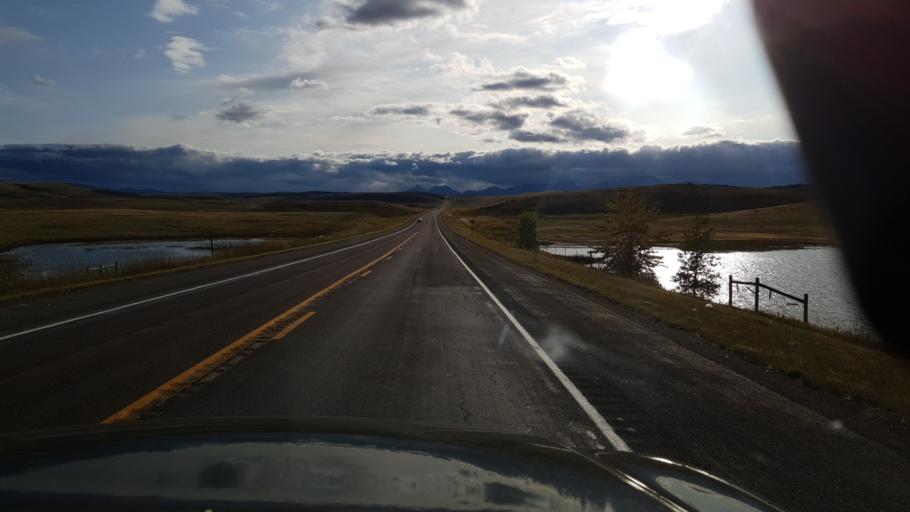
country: US
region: Montana
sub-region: Glacier County
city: South Browning
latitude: 48.5376
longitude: -113.0412
